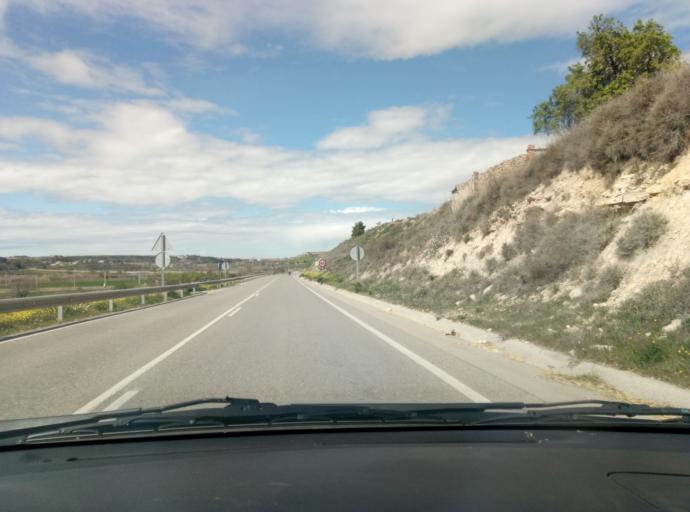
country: ES
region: Catalonia
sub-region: Provincia de Lleida
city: Vallbona de les Monges
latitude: 41.5577
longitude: 1.0528
